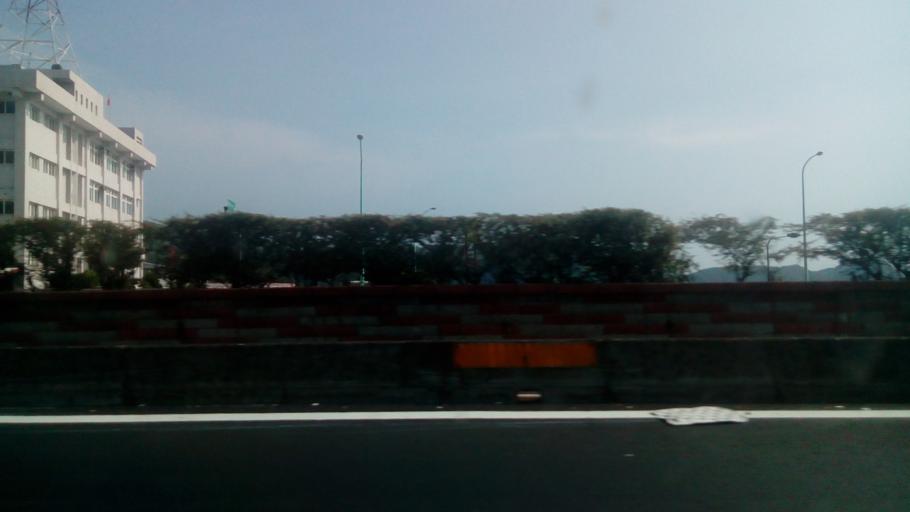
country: TW
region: Taiwan
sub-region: Yilan
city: Yilan
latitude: 24.5946
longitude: 121.8579
